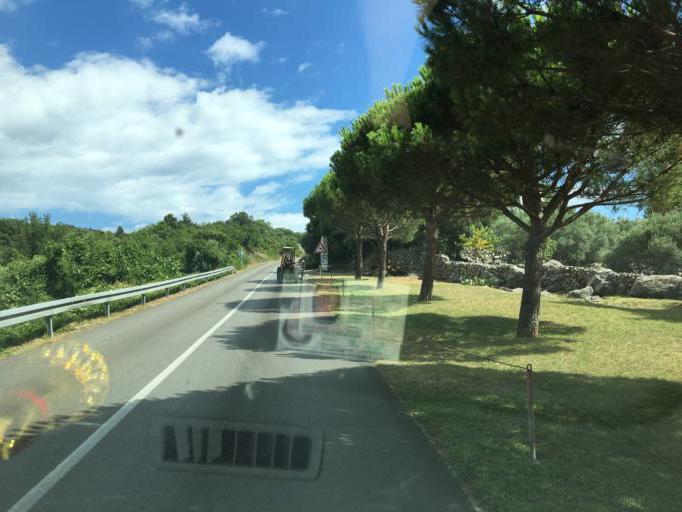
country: HR
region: Primorsko-Goranska
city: Punat
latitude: 45.0257
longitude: 14.6316
